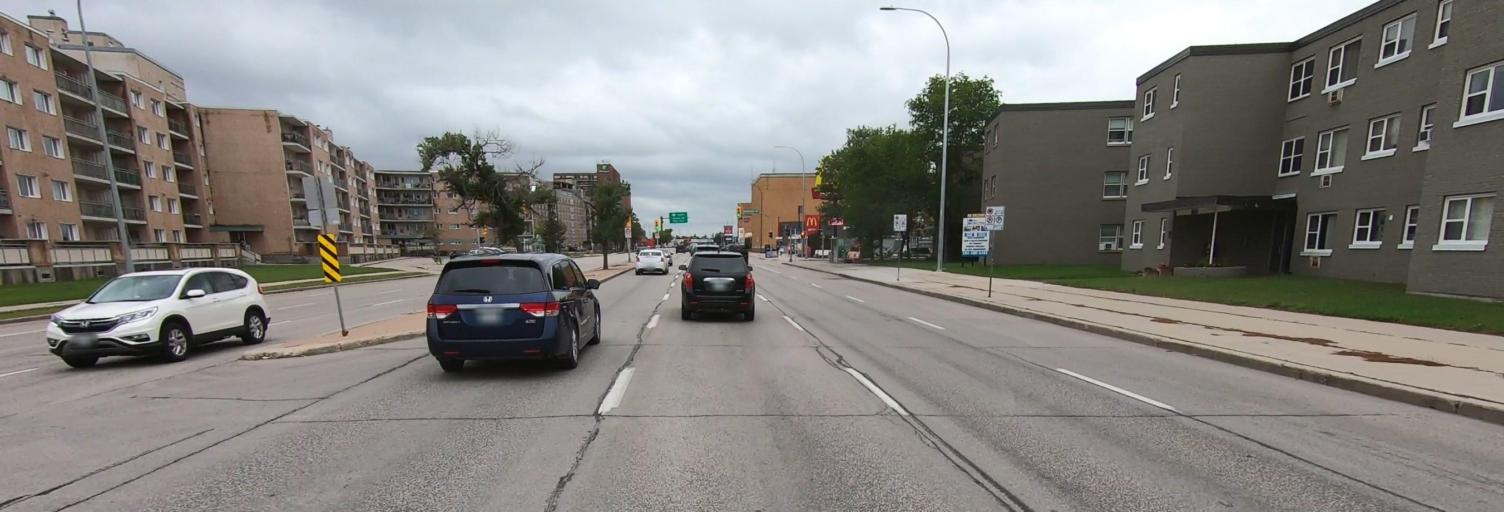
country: CA
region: Manitoba
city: Winnipeg
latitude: 49.8756
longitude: -97.2537
